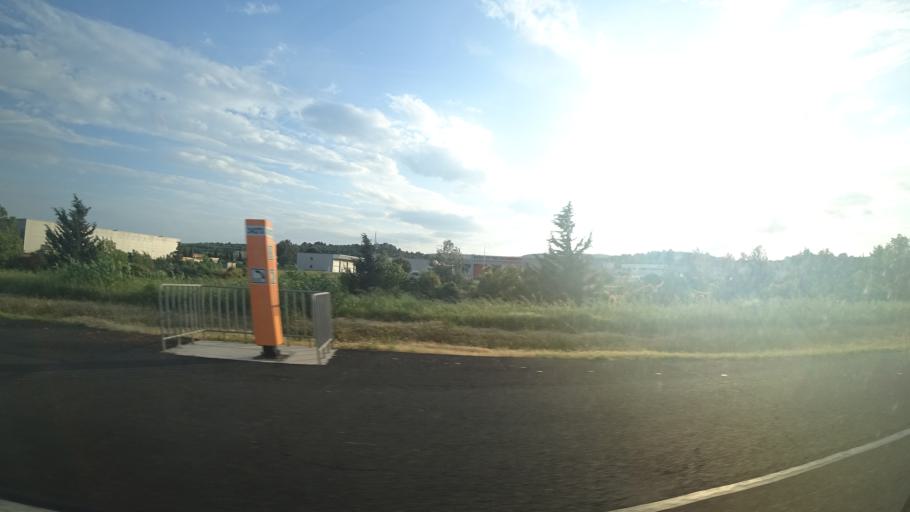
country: FR
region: Languedoc-Roussillon
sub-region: Departement de l'Herault
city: Nebian
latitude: 43.6212
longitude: 3.4558
